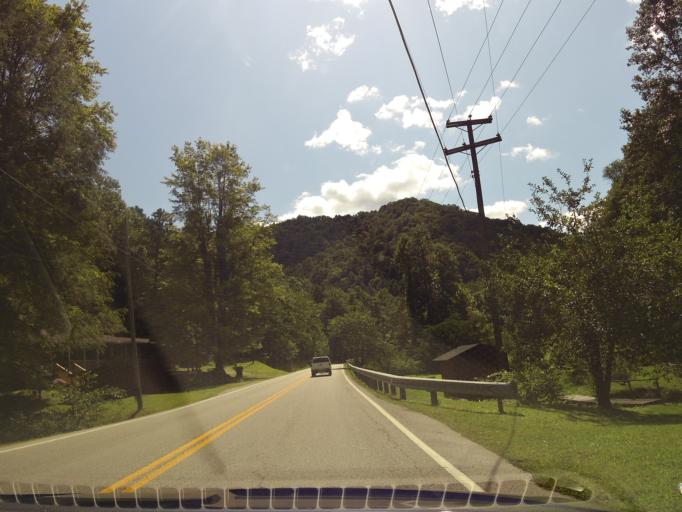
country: US
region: Kentucky
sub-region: Leslie County
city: Hyden
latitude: 37.0283
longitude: -83.3896
